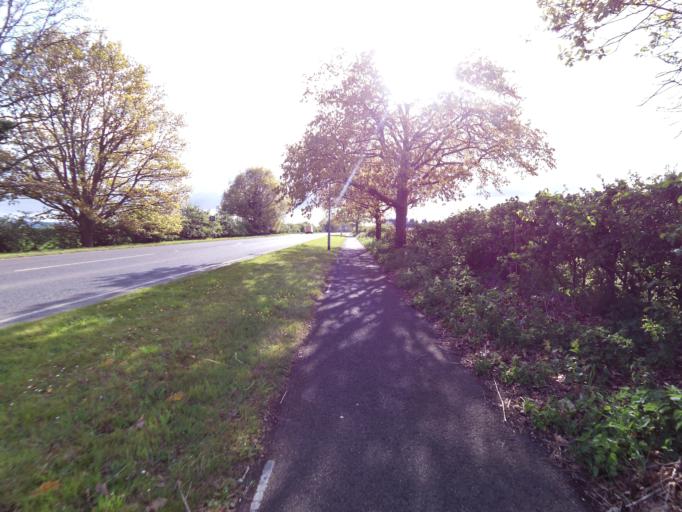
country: GB
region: England
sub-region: Cambridgeshire
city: Fulbourn
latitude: 52.2171
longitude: 0.2230
